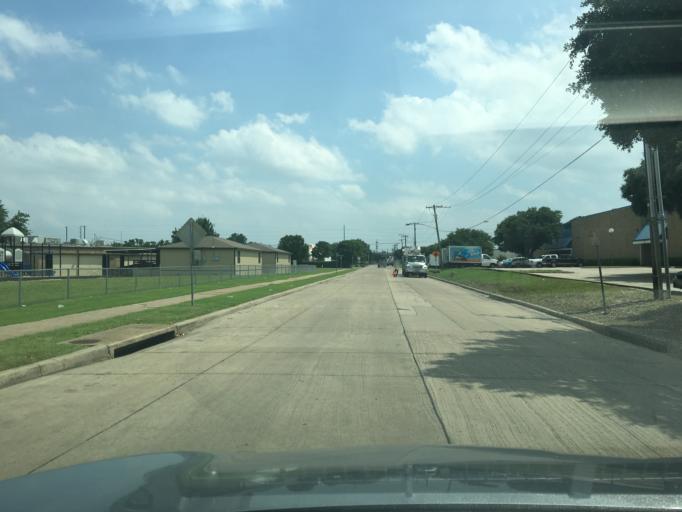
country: US
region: Texas
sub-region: Dallas County
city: Garland
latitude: 32.9153
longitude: -96.6769
